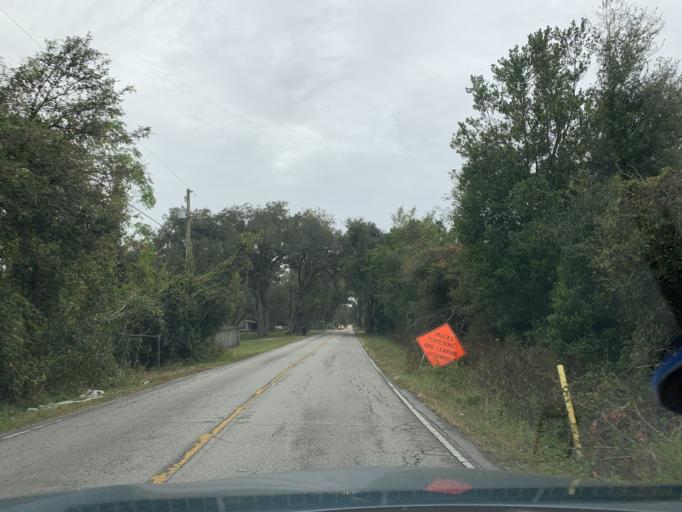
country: US
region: Florida
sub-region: Pasco County
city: Zephyrhills North
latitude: 28.2837
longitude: -82.1797
